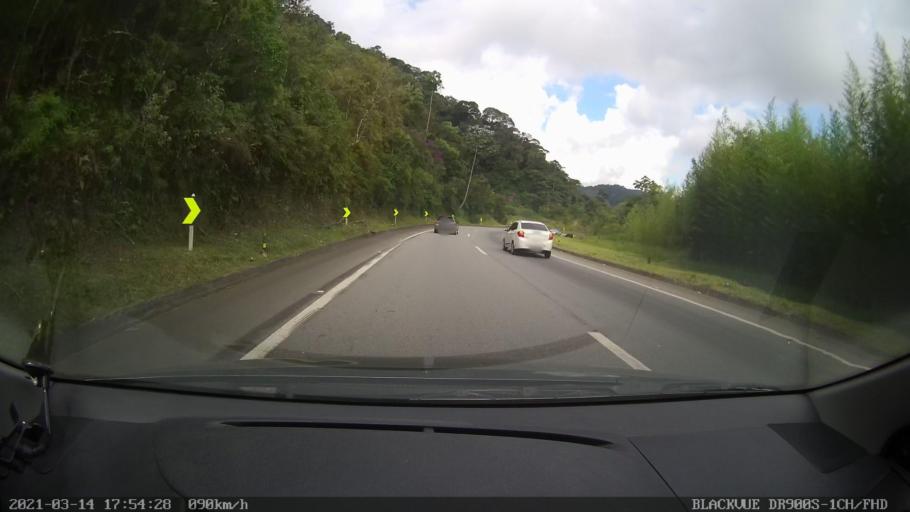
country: BR
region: Rio de Janeiro
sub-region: Petropolis
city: Petropolis
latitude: -22.4870
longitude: -43.2253
